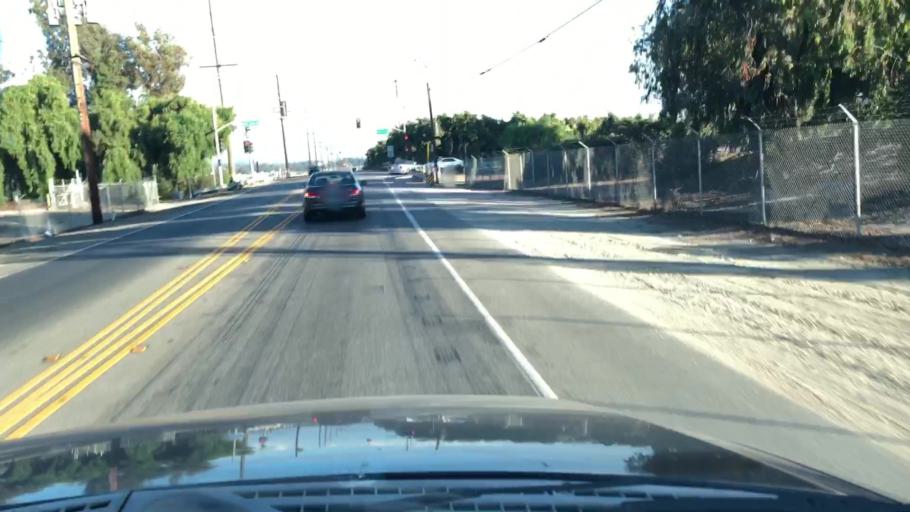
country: US
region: California
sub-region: Ventura County
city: Saticoy
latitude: 34.2684
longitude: -119.1273
